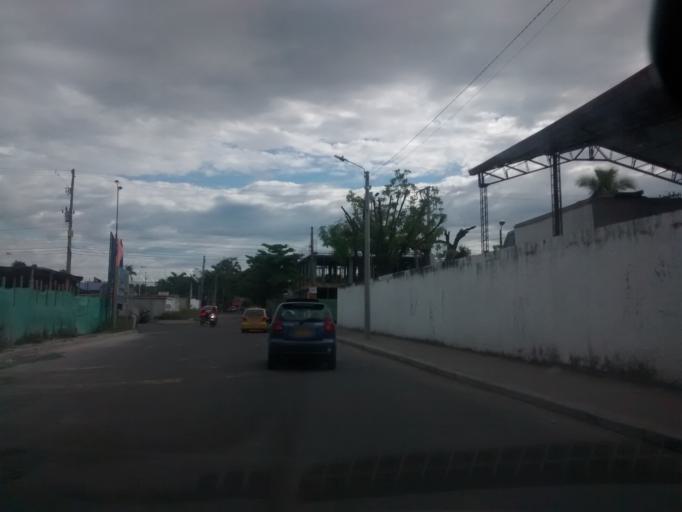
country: CO
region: Cundinamarca
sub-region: Girardot
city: Girardot City
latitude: 4.3056
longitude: -74.8020
